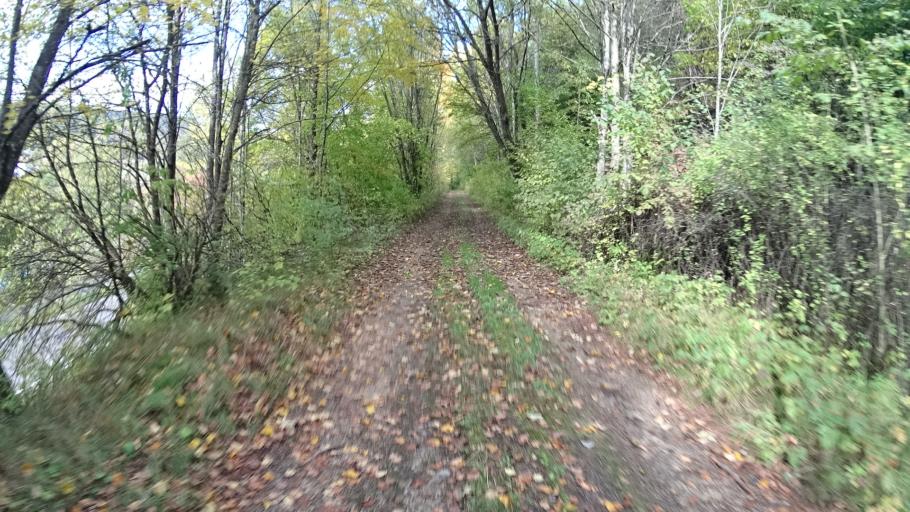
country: DE
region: Bavaria
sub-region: Upper Bavaria
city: Walting
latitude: 48.9120
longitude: 11.3058
